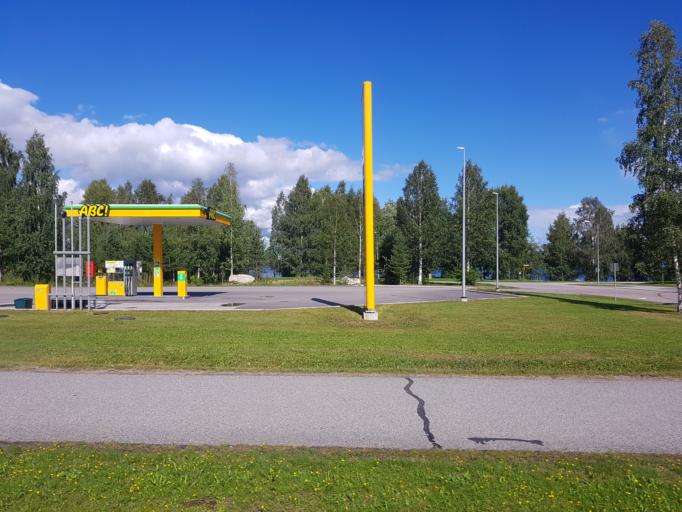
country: FI
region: Kainuu
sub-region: Kajaani
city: Sotkamo
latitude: 64.1313
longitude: 28.3623
